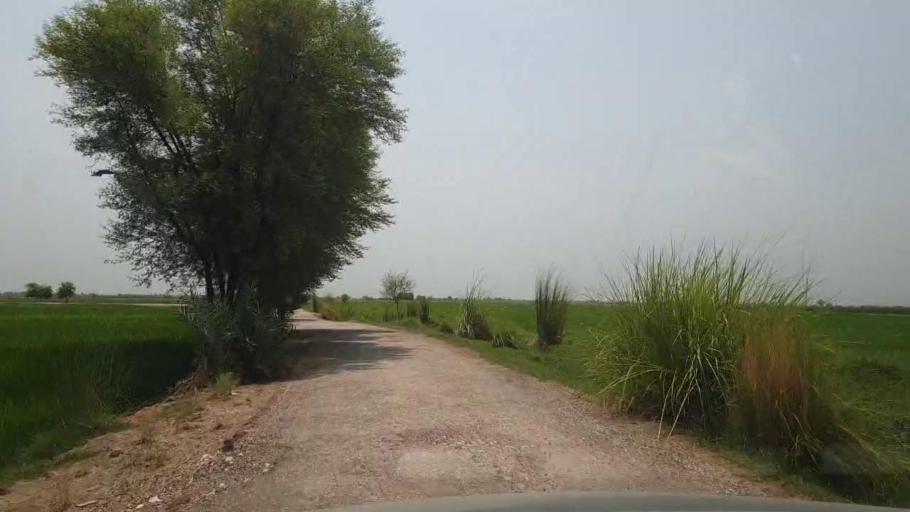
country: PK
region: Sindh
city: Garhi Yasin
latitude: 27.8707
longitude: 68.5012
